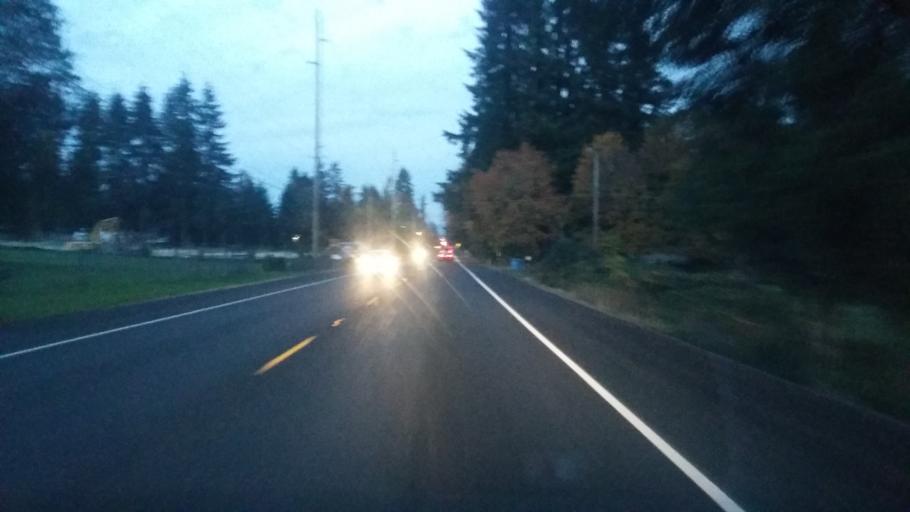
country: US
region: Washington
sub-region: Clark County
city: Barberton
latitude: 45.7176
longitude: -122.5994
